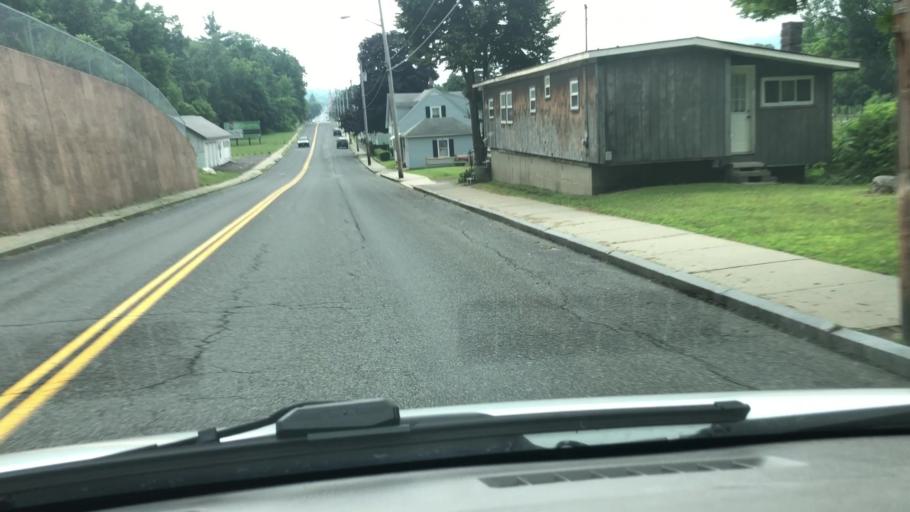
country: US
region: Massachusetts
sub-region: Berkshire County
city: Adams
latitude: 42.6366
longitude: -73.1084
